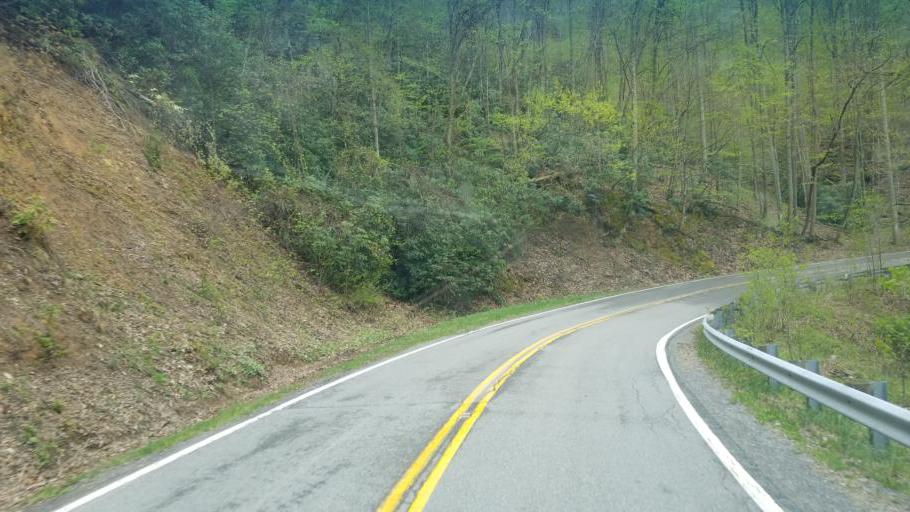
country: US
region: Virginia
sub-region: Tazewell County
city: Tazewell
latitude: 37.0040
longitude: -81.5217
